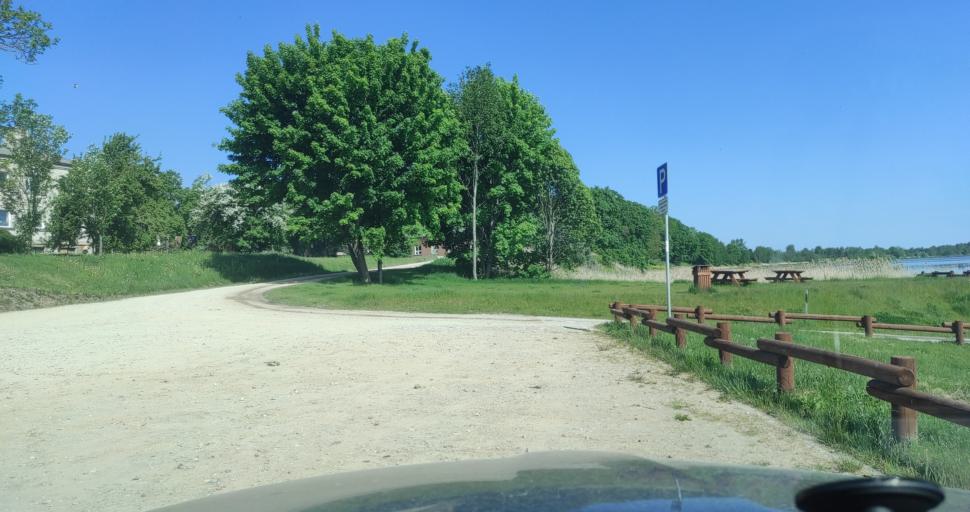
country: LV
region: Ventspils
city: Ventspils
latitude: 57.3054
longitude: 21.5639
